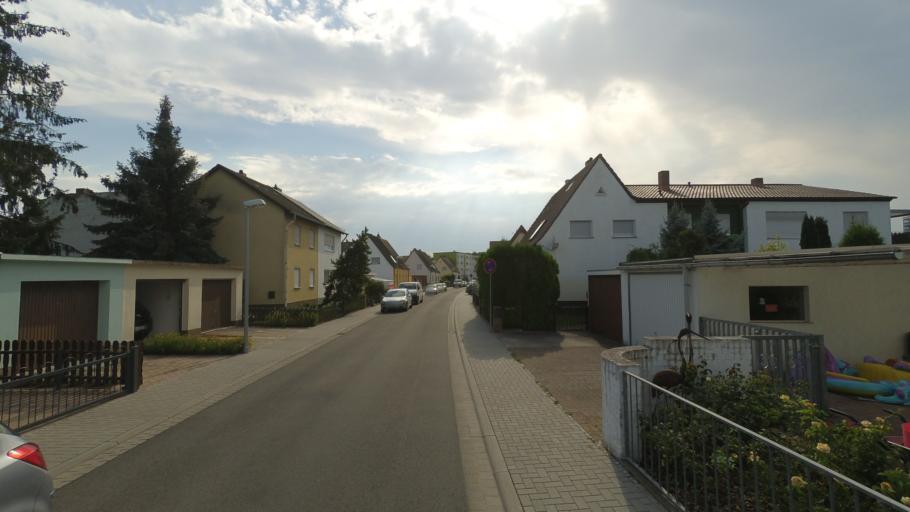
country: DE
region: Rheinland-Pfalz
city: Gartenstadt
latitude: 49.4750
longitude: 8.4008
